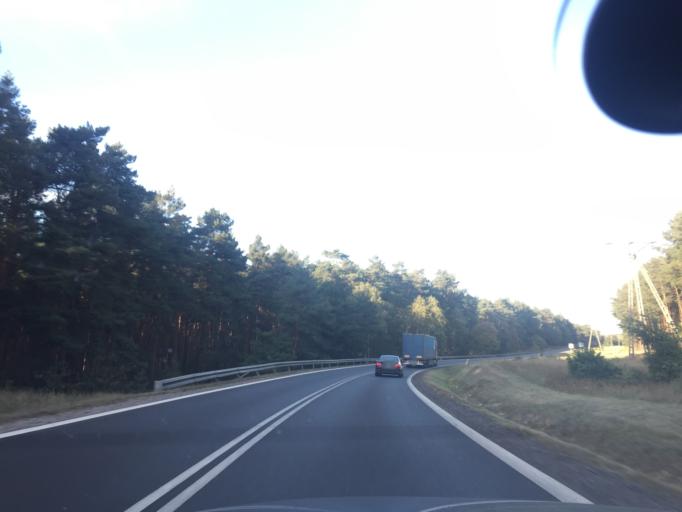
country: PL
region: Kujawsko-Pomorskie
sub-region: Powiat torunski
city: Wielka Nieszawka
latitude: 52.9238
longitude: 18.4997
